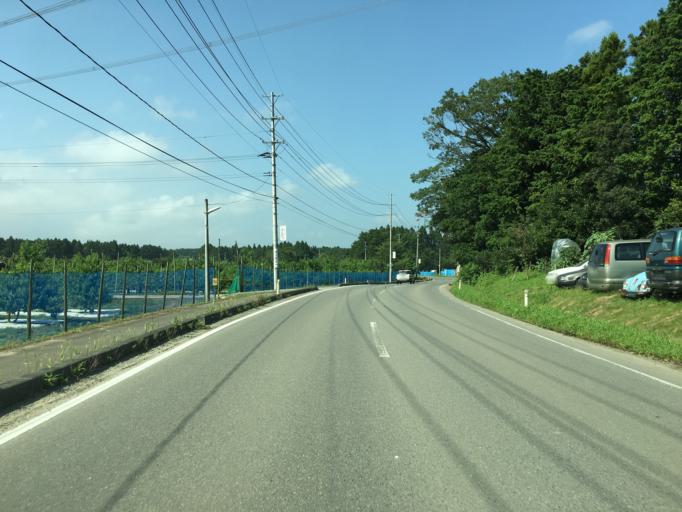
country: JP
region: Miyagi
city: Marumori
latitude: 37.8531
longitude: 140.8956
